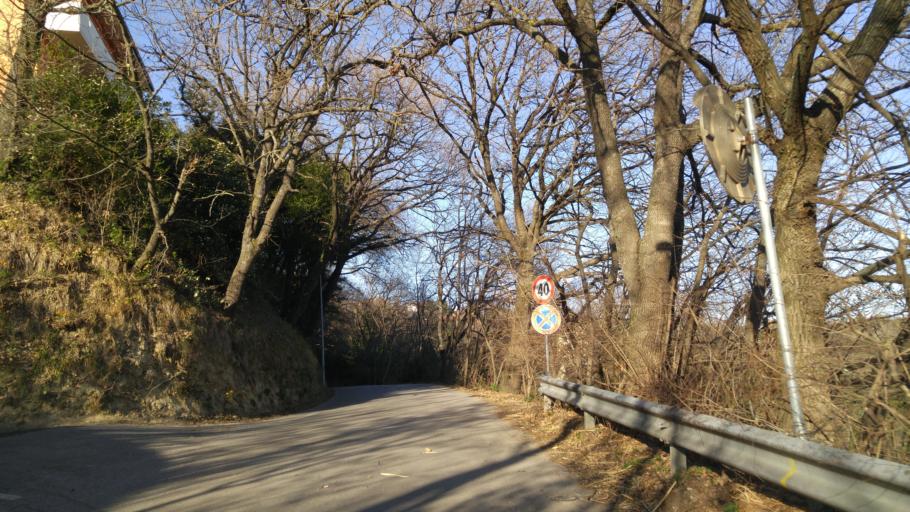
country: IT
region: The Marches
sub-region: Provincia di Pesaro e Urbino
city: Fenile
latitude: 43.8566
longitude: 12.9290
